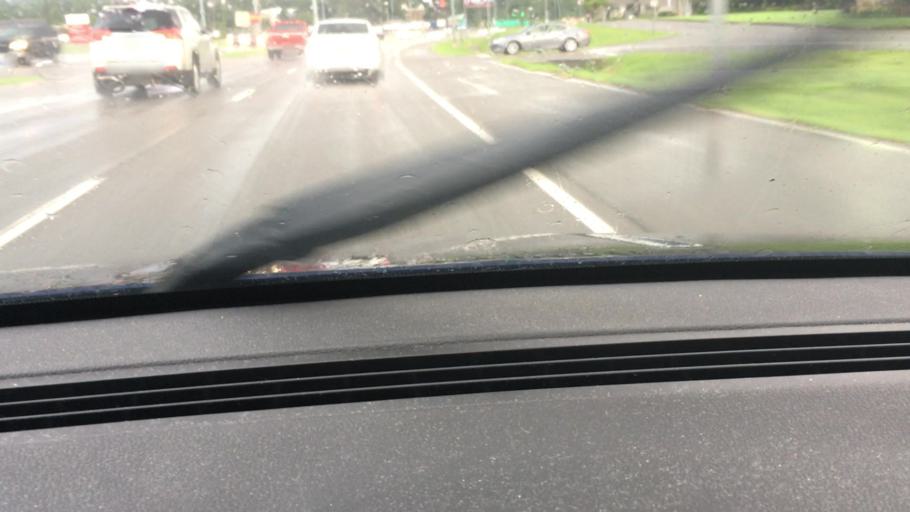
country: US
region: Alabama
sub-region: Tuscaloosa County
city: Tuscaloosa
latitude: 33.2306
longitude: -87.5351
